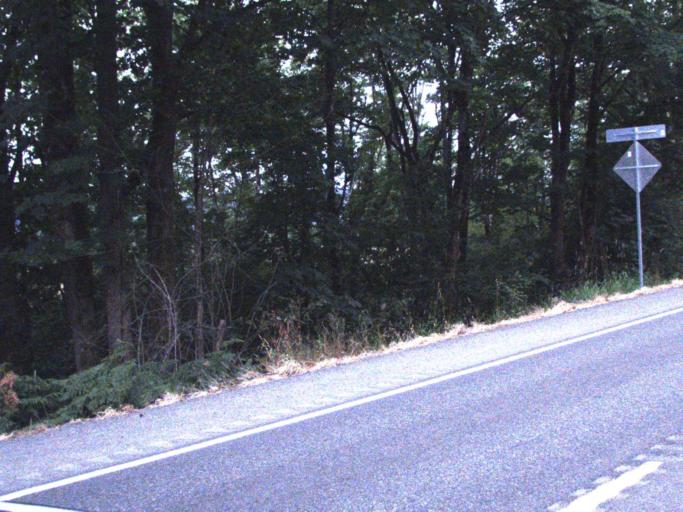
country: US
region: Washington
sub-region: King County
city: Duvall
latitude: 47.7836
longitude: -121.9682
